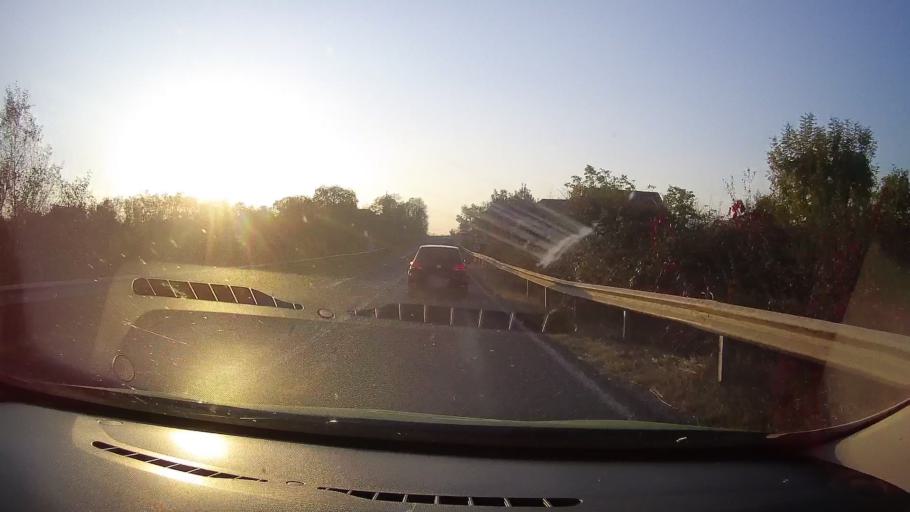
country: RO
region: Arad
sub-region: Comuna Bocsig
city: Bocsig
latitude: 46.4159
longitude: 21.9892
